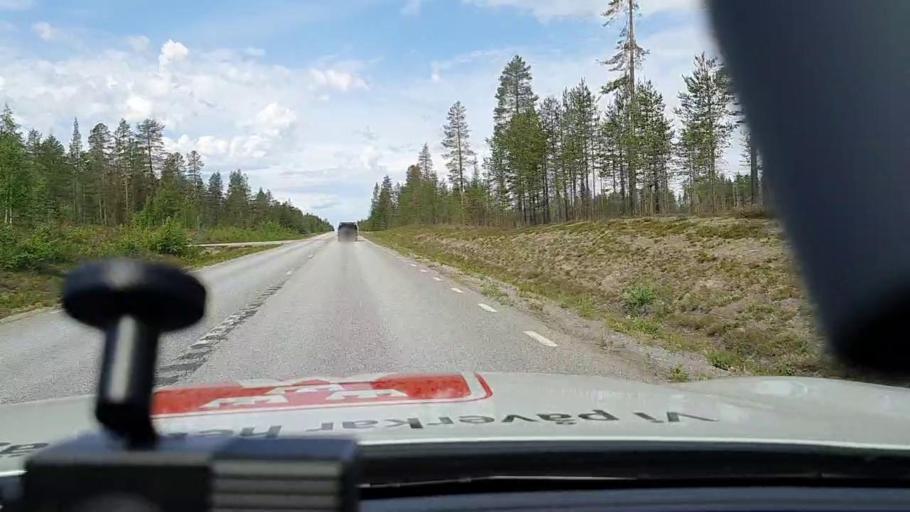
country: SE
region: Norrbotten
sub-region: Jokkmokks Kommun
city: Jokkmokk
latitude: 66.5234
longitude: 20.2045
